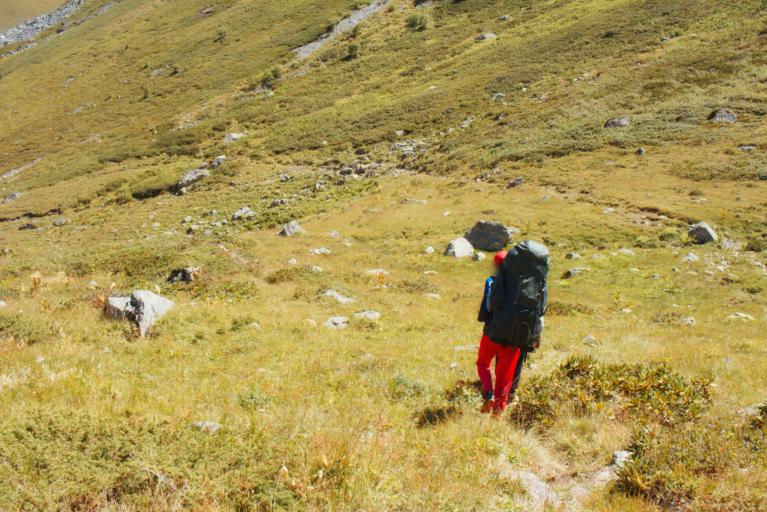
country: RU
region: Karachayevo-Cherkesiya
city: Mednogorskiy
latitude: 43.6320
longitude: 41.1304
